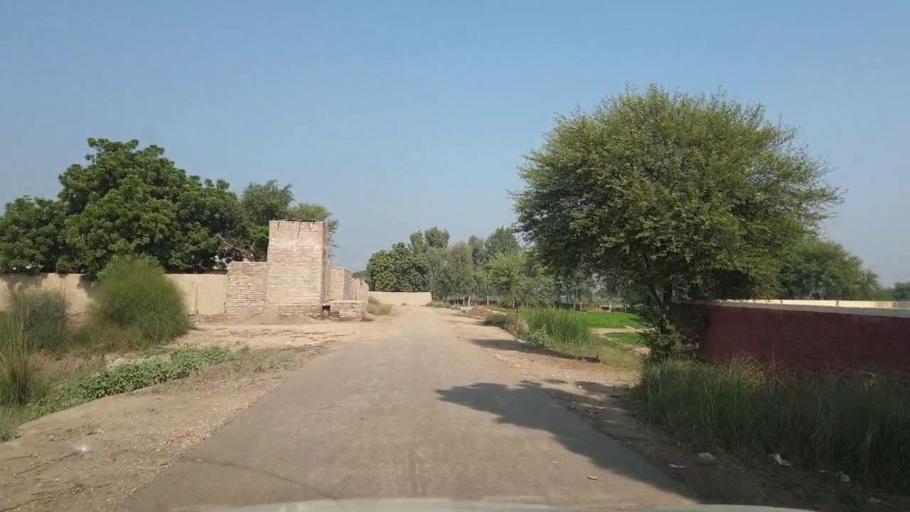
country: PK
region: Sindh
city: Bhan
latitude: 26.4881
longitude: 67.7817
